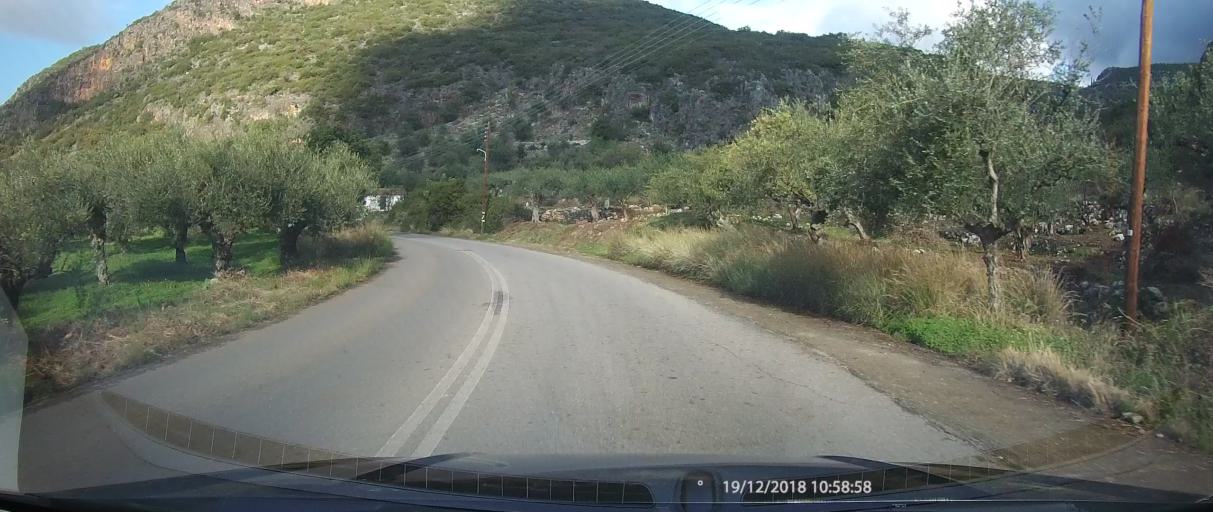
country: GR
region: Peloponnese
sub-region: Nomos Messinias
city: Kardamyli
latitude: 36.8975
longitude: 22.2312
